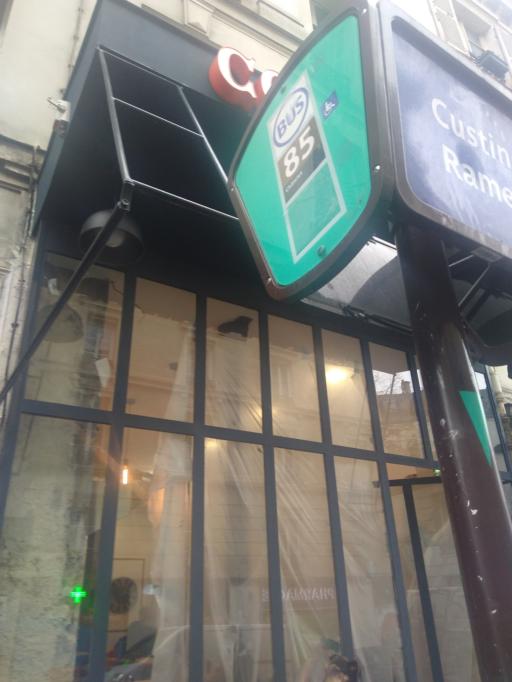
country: FR
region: Ile-de-France
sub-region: Paris
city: Saint-Ouen
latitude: 48.8885
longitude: 2.3467
